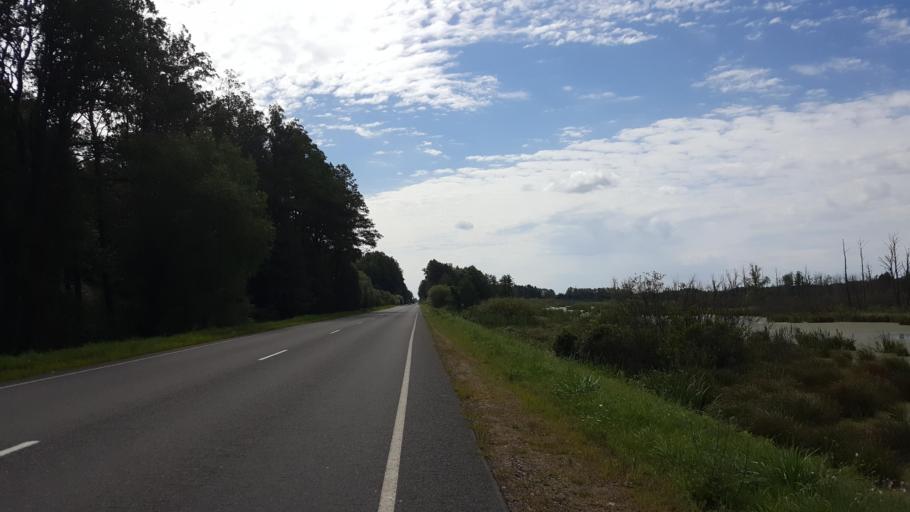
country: BY
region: Brest
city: Zhabinka
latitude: 52.2740
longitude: 23.9531
